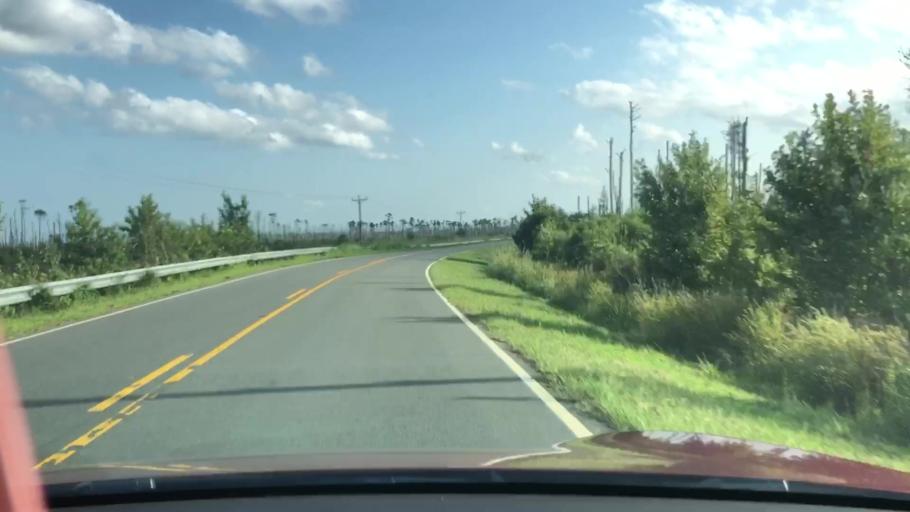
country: US
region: North Carolina
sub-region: Dare County
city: Wanchese
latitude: 35.6443
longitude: -75.7772
